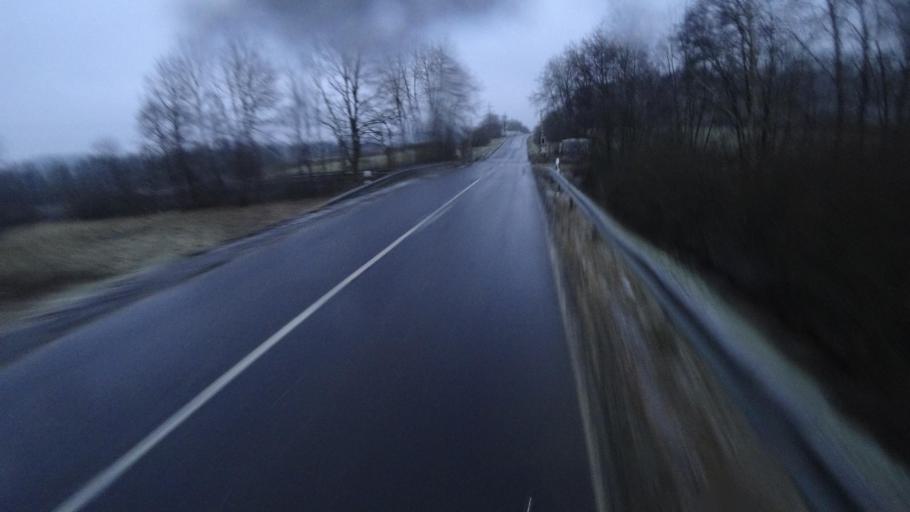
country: DE
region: Rheinland-Pfalz
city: Bellingen
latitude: 50.5966
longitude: 7.8921
